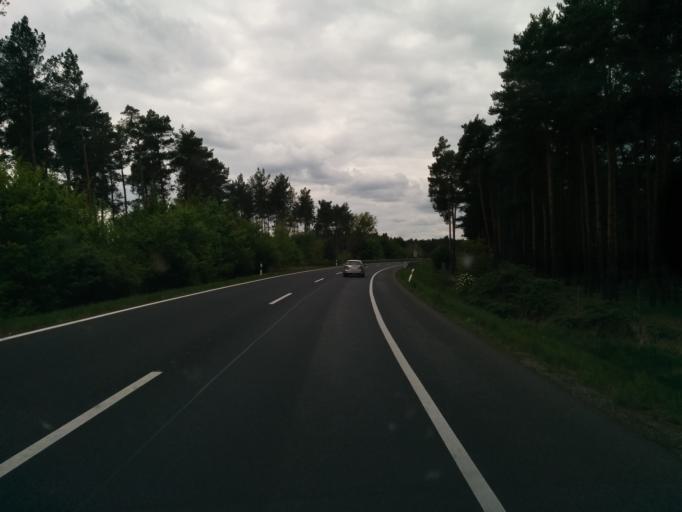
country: DE
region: Brandenburg
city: Gross Kreutz
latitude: 52.3391
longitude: 12.8115
